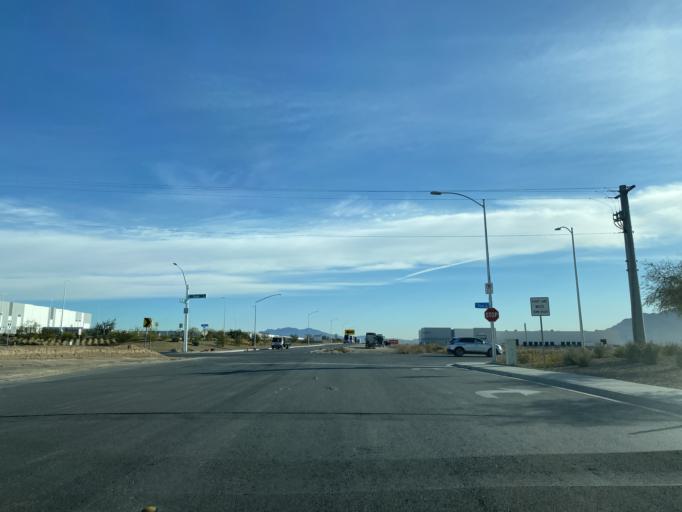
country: US
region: Nevada
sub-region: Clark County
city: Nellis Air Force Base
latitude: 36.2623
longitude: -115.0439
